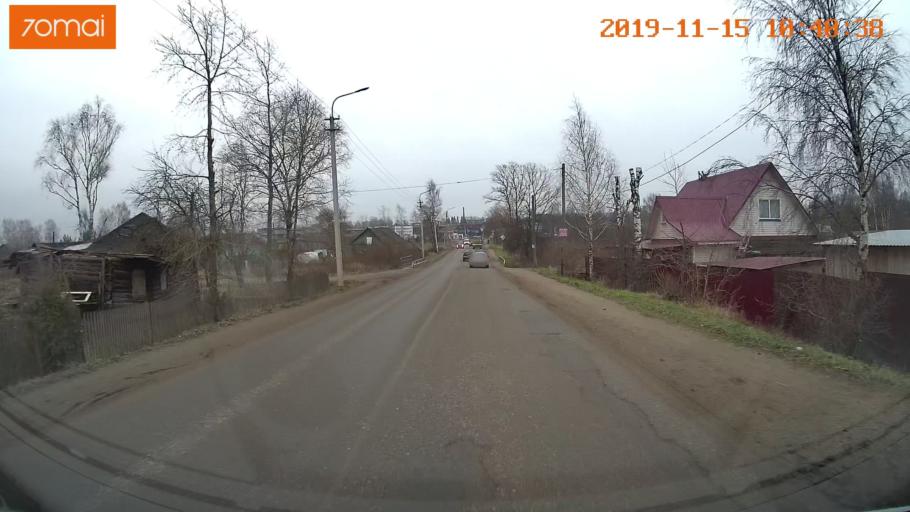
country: RU
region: Vologda
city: Sheksna
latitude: 59.2130
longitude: 38.5099
